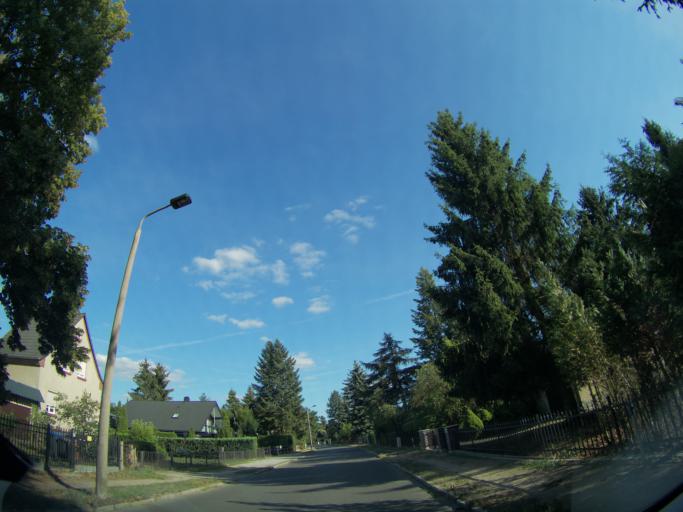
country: DE
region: Brandenburg
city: Stahnsdorf
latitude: 52.3836
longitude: 13.1939
